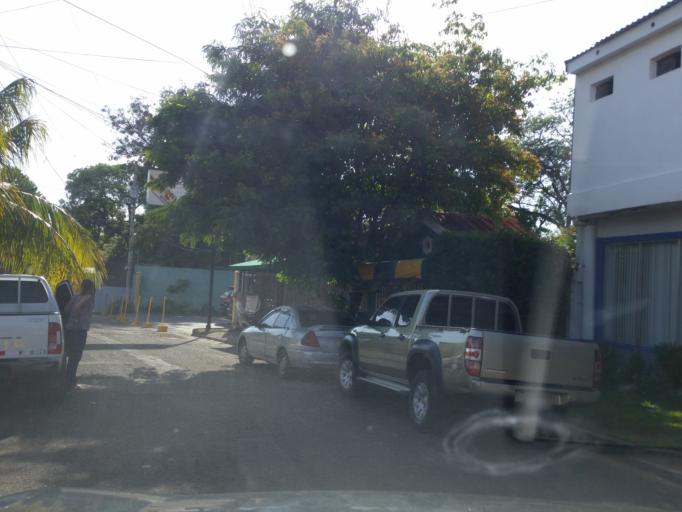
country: NI
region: Managua
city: Managua
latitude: 12.1227
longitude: -86.2664
